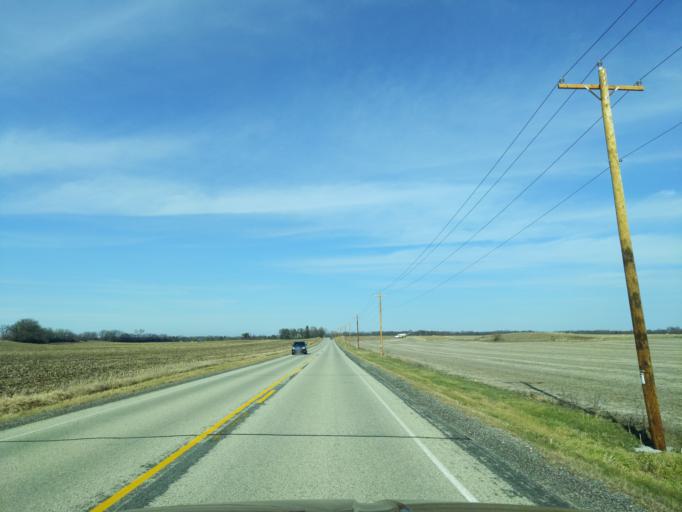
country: US
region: Wisconsin
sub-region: Walworth County
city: Elkhorn
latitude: 42.7386
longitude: -88.5922
